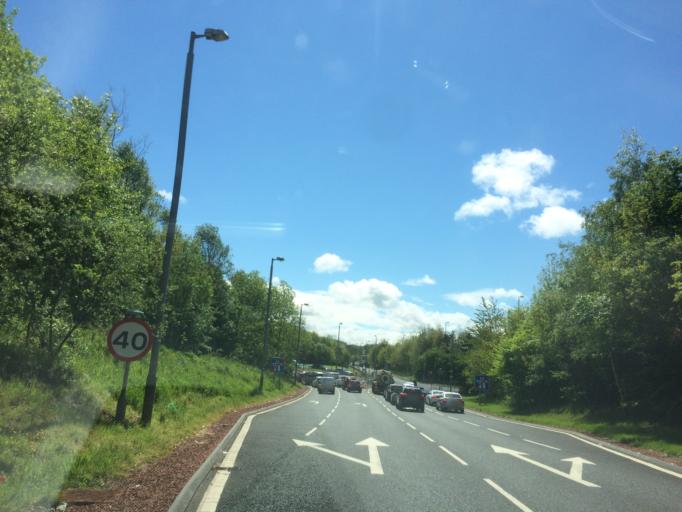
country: GB
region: Scotland
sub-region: East Renfrewshire
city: Newton Mearns
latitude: 55.8054
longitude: -4.3358
